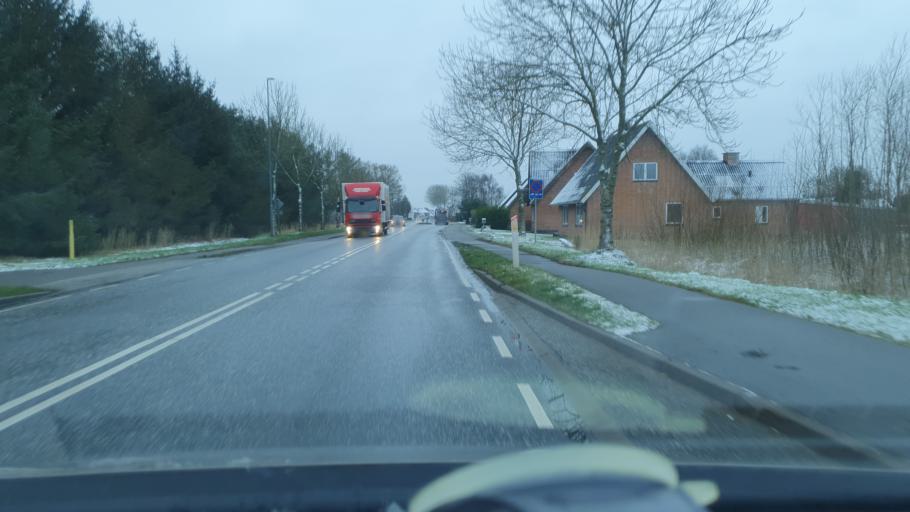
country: DK
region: North Denmark
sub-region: Jammerbugt Kommune
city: Brovst
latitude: 57.1126
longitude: 9.5969
